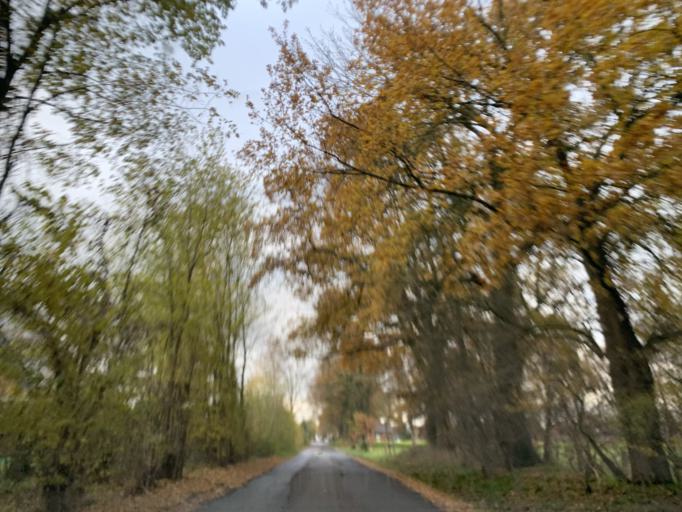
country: DE
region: North Rhine-Westphalia
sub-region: Regierungsbezirk Munster
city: Laer
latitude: 52.1061
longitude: 7.3944
